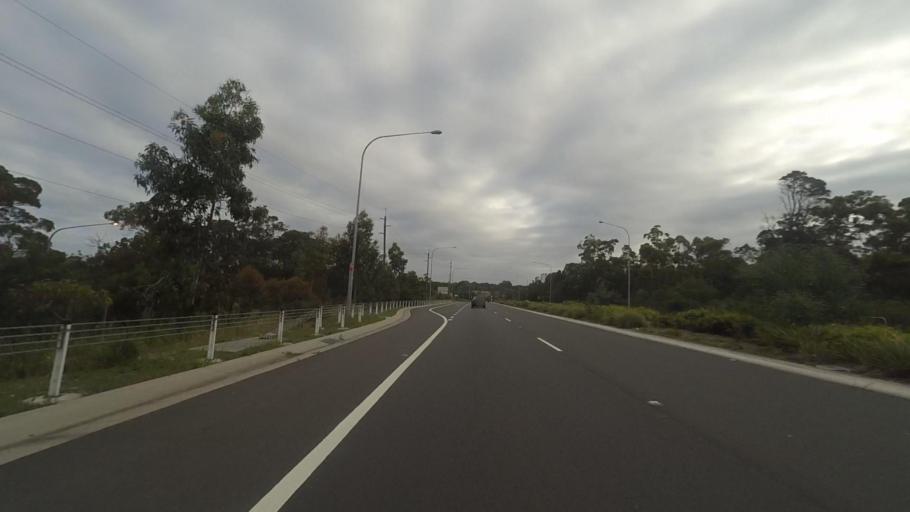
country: AU
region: New South Wales
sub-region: Sutherland Shire
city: Menai
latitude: -34.0305
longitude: 151.0060
